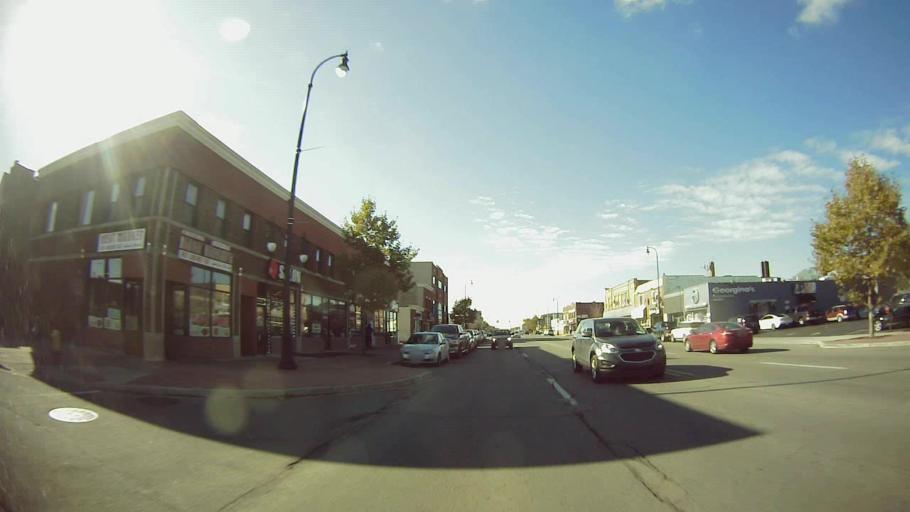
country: US
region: Michigan
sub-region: Wayne County
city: Dearborn
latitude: 42.3443
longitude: -83.1647
